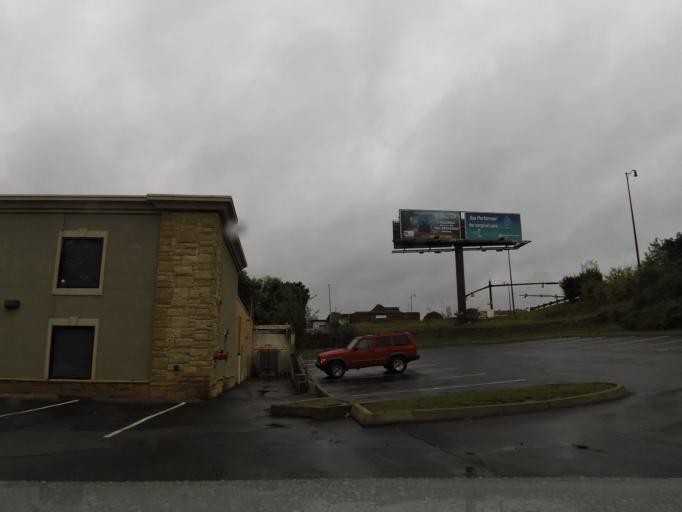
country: US
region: Tennessee
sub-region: Blount County
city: Maryville
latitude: 35.7611
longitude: -83.9671
